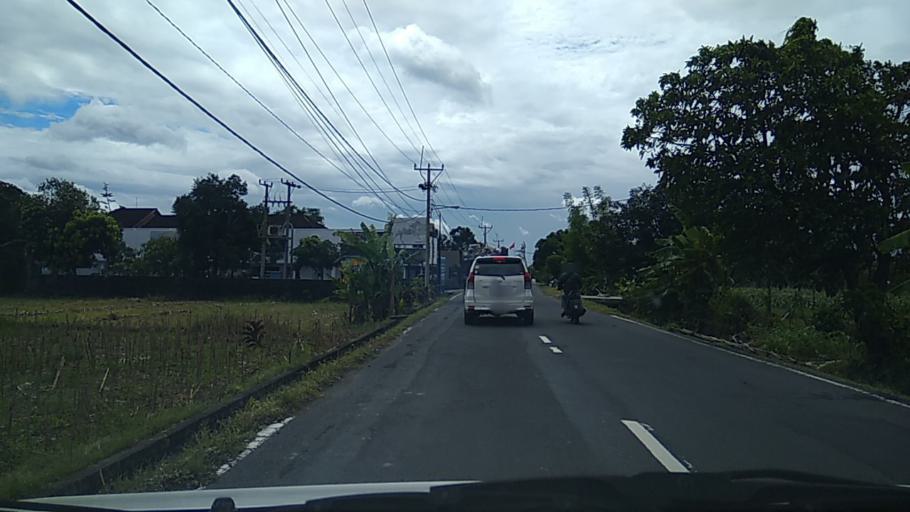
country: ID
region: Bali
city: Dajan Tangluk
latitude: -8.6527
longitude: 115.2511
